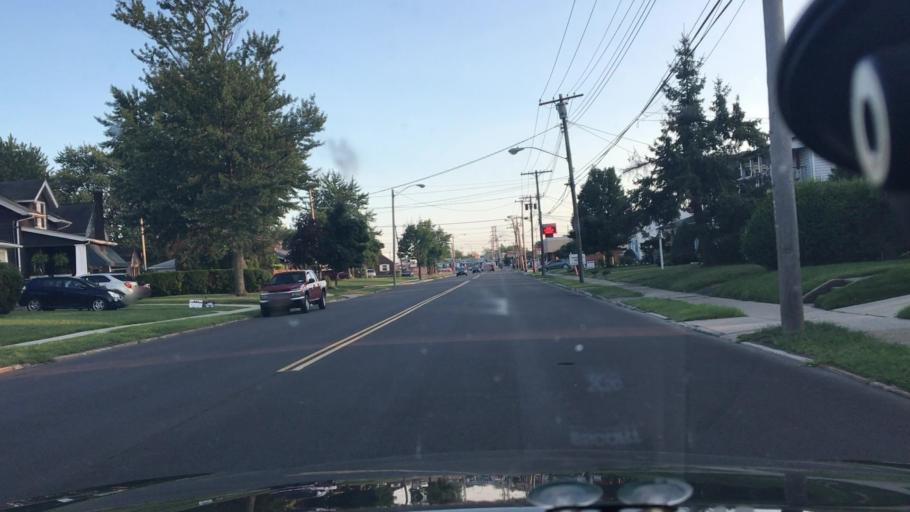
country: US
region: New York
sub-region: Erie County
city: Tonawanda
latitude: 43.0042
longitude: -78.8747
